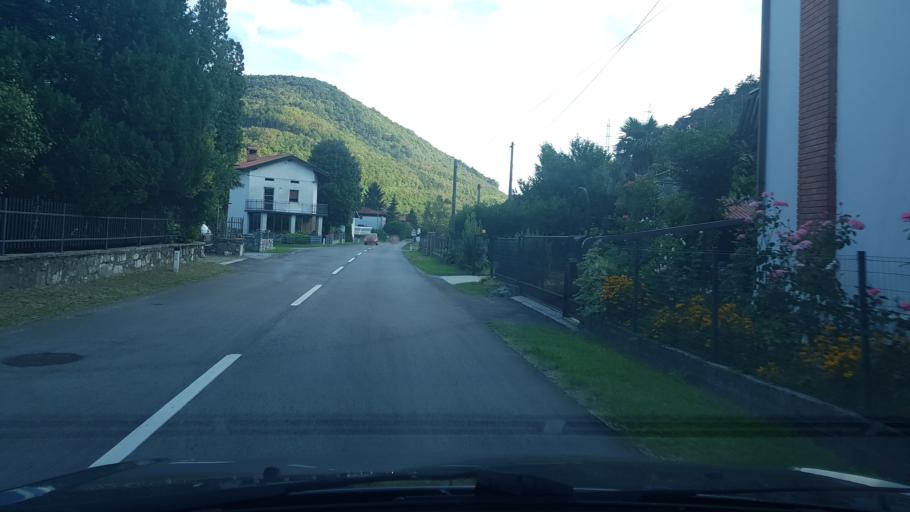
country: SI
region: Nova Gorica
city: Solkan
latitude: 45.9959
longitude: 13.6725
